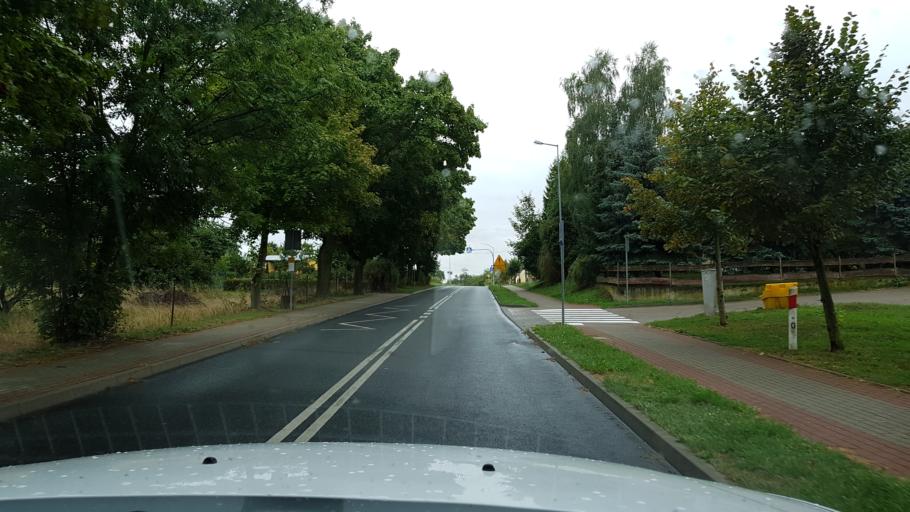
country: PL
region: West Pomeranian Voivodeship
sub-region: Powiat gryfinski
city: Cedynia
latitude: 52.8794
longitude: 14.2134
